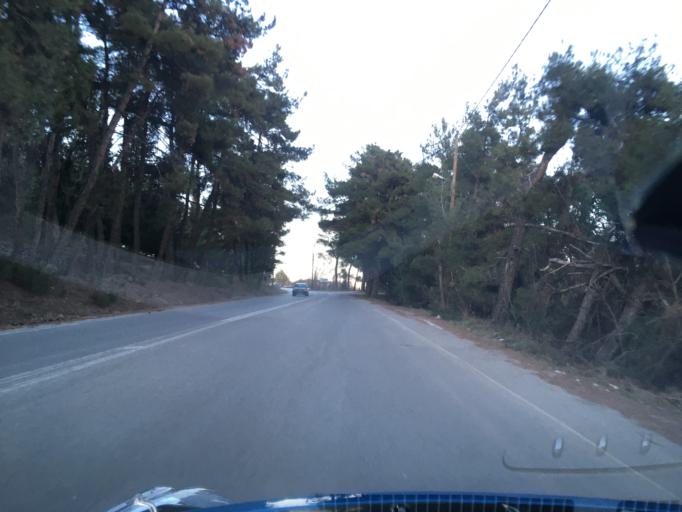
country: GR
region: West Macedonia
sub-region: Nomos Kozanis
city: Kozani
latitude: 40.2756
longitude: 21.7823
